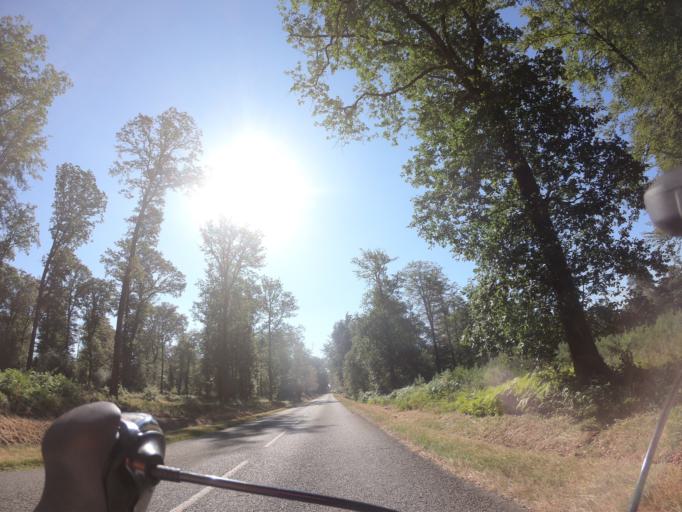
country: FR
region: Lower Normandy
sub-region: Departement de l'Orne
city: Tesse-la-Madeleine
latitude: 48.5753
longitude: -0.4599
